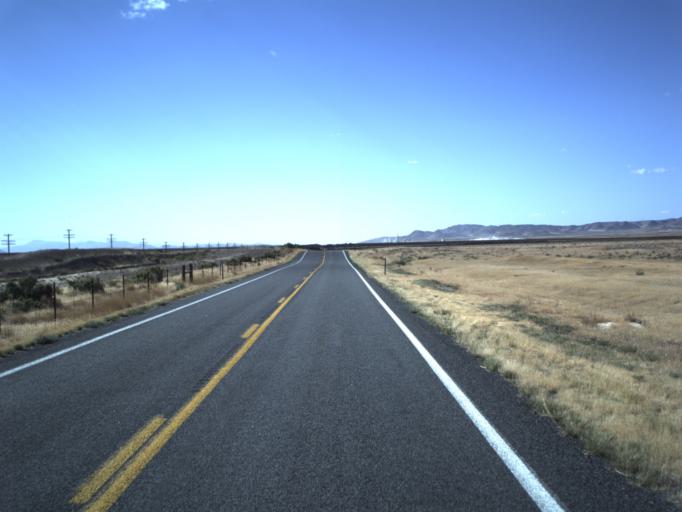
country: US
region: Utah
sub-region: Millard County
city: Delta
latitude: 38.9864
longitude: -112.7930
